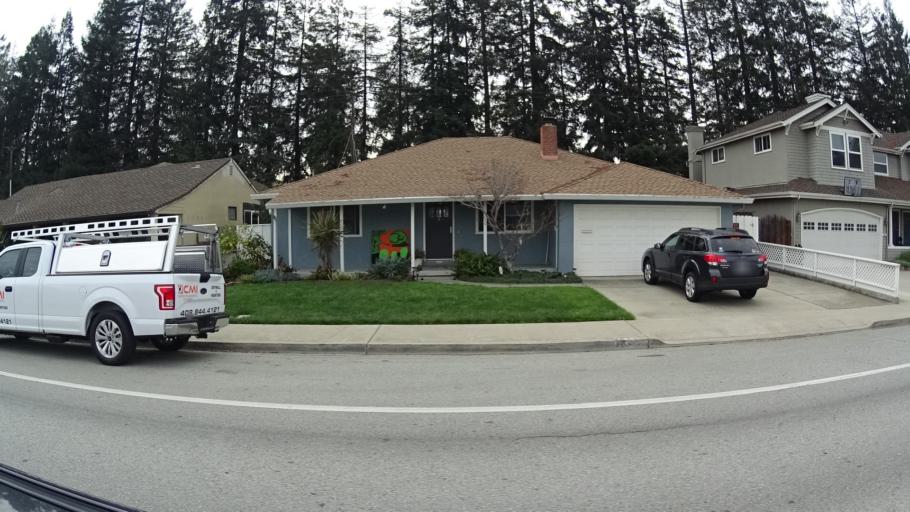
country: US
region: California
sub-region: Santa Clara County
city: Santa Clara
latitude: 37.3344
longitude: -121.9589
